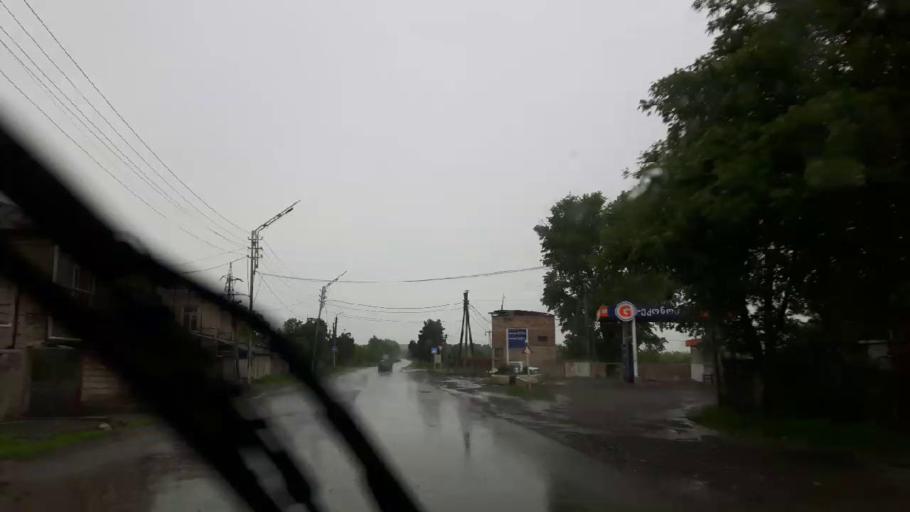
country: GE
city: Agara
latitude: 42.0138
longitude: 43.8624
